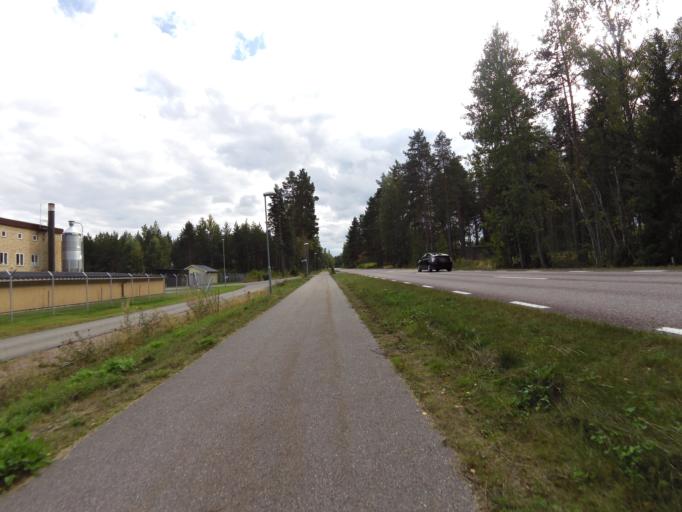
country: SE
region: Gaevleborg
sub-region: Sandvikens Kommun
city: Sandviken
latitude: 60.6881
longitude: 16.8145
